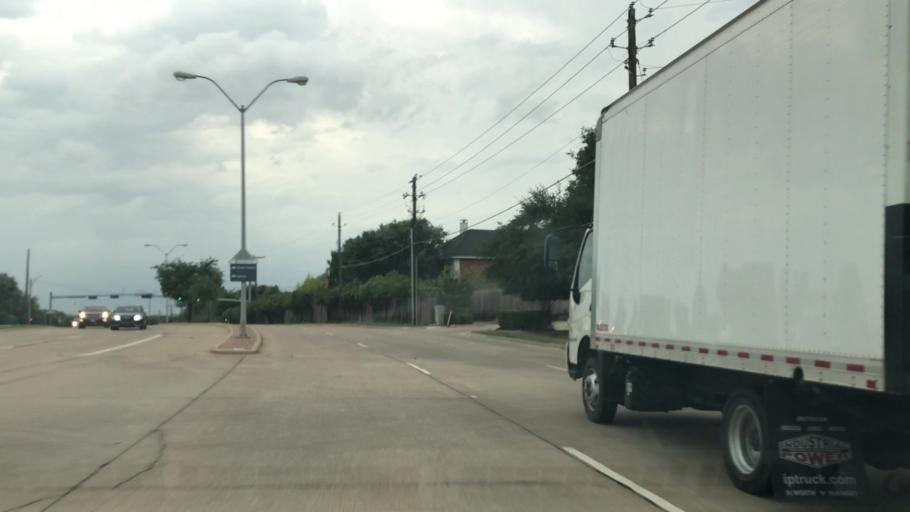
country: US
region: Texas
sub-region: Dallas County
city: Carrollton
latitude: 32.9727
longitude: -96.8932
